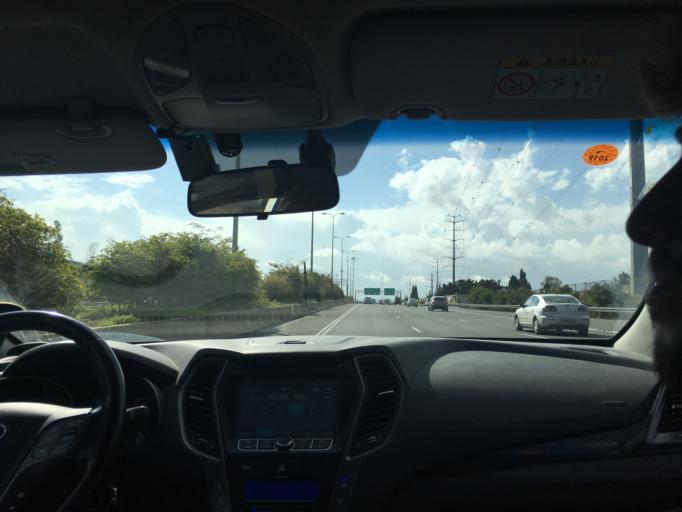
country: IL
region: Tel Aviv
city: Azor
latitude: 32.0452
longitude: 34.8297
